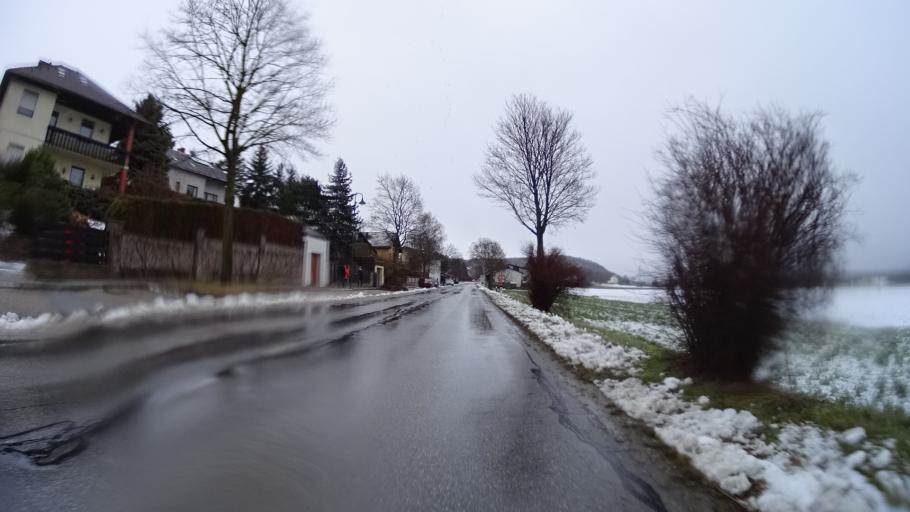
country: AT
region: Lower Austria
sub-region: Politischer Bezirk Korneuburg
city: Leobendorf
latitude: 48.3807
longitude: 16.2867
